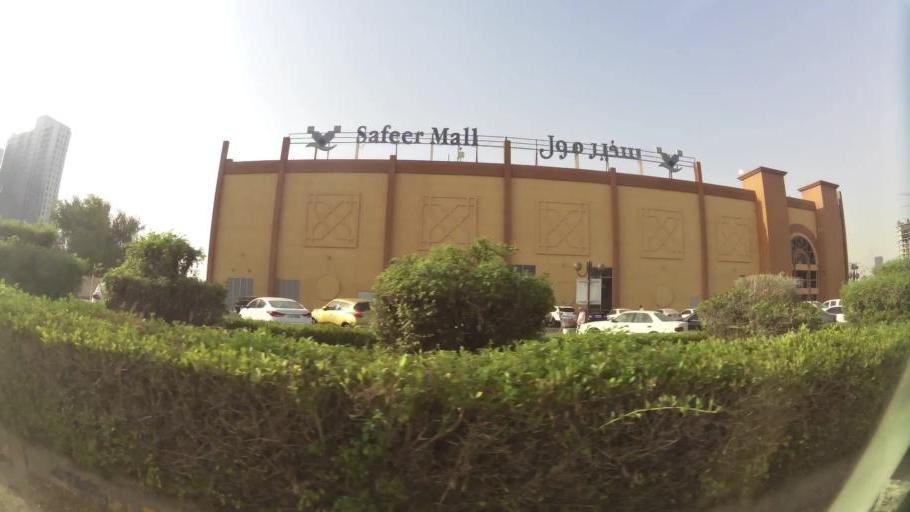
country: AE
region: Ajman
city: Ajman
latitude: 25.3893
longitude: 55.4446
